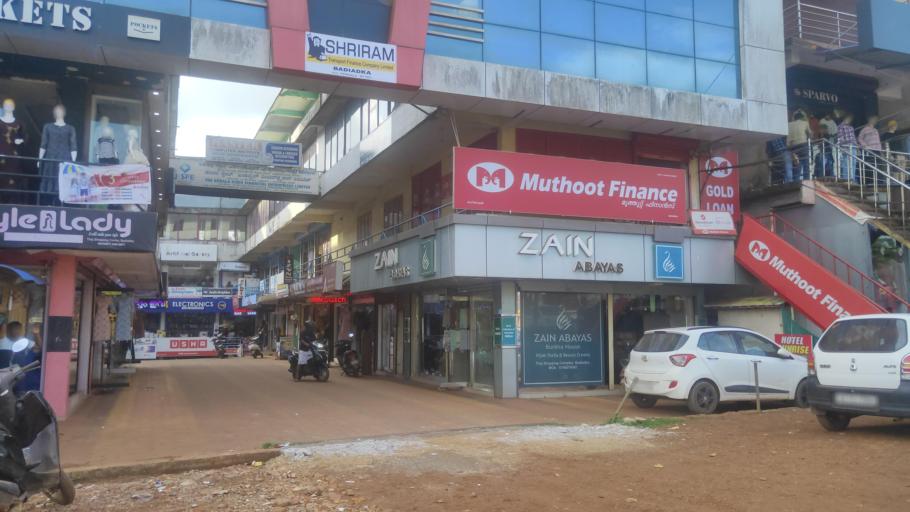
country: IN
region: Kerala
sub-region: Kasaragod District
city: Kasaragod
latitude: 12.5887
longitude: 75.0714
